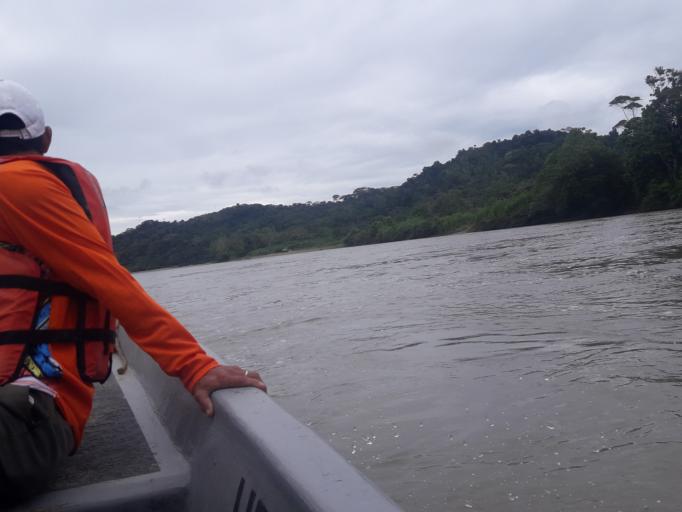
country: EC
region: Orellana
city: Boca Suno
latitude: -0.8811
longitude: -77.2823
